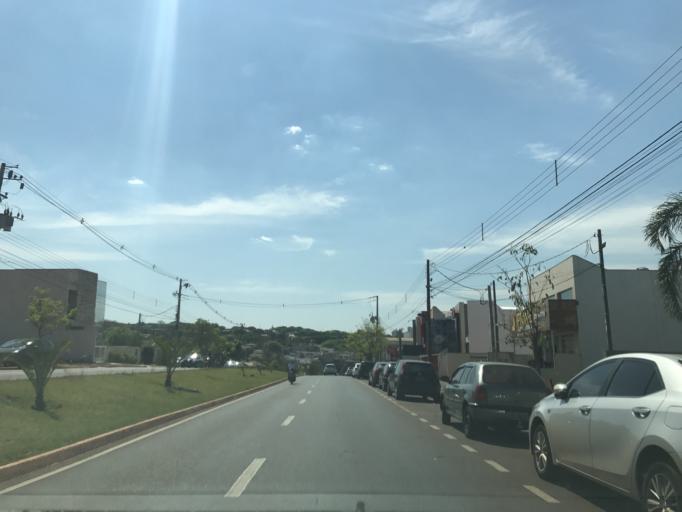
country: BR
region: Parana
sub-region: Maringa
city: Maringa
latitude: -23.4440
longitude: -51.9449
